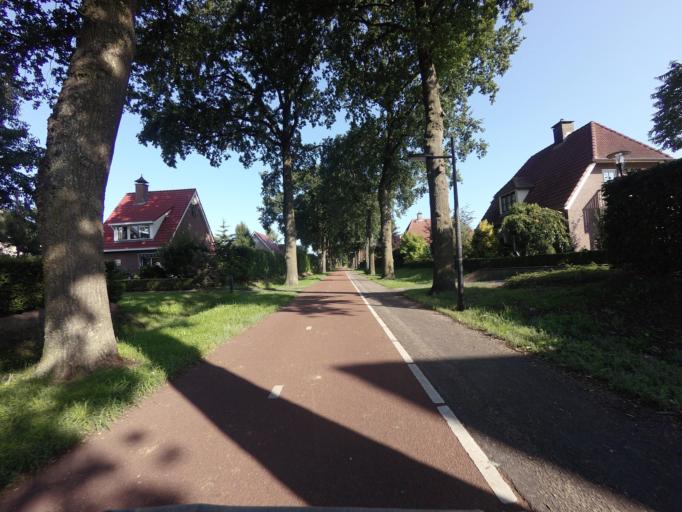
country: NL
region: Overijssel
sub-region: Gemeente Raalte
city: Raalte
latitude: 52.3969
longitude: 6.2842
